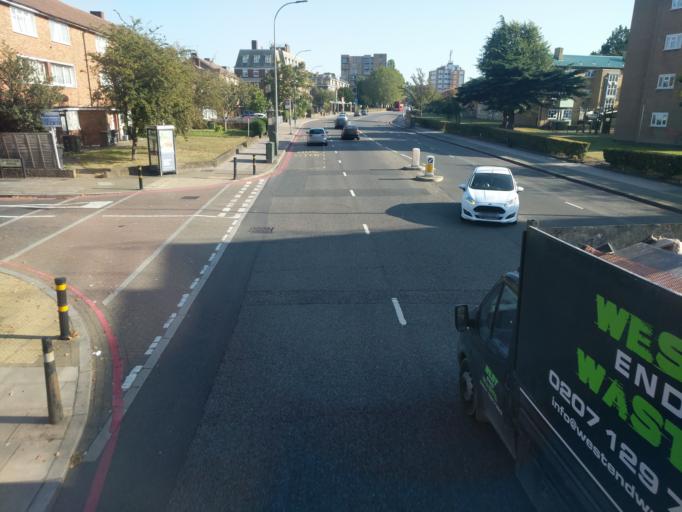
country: GB
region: England
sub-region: Greater London
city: Catford
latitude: 51.4317
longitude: -0.0163
